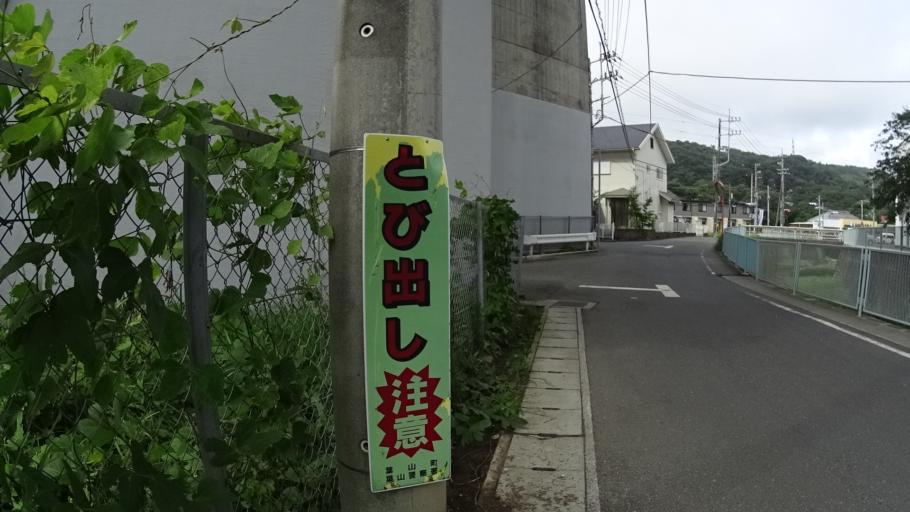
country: JP
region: Kanagawa
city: Yokosuka
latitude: 35.2647
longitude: 139.6323
